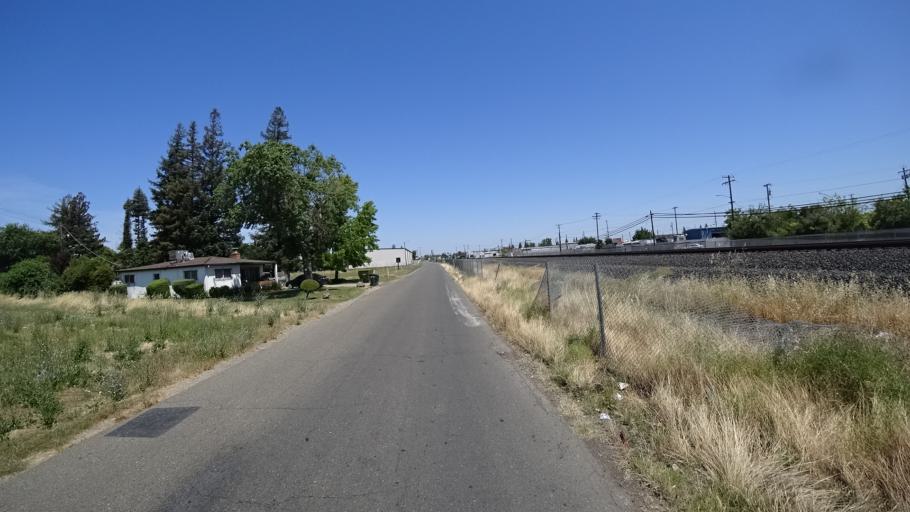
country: US
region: California
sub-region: Sacramento County
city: Florin
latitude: 38.5358
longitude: -121.4123
